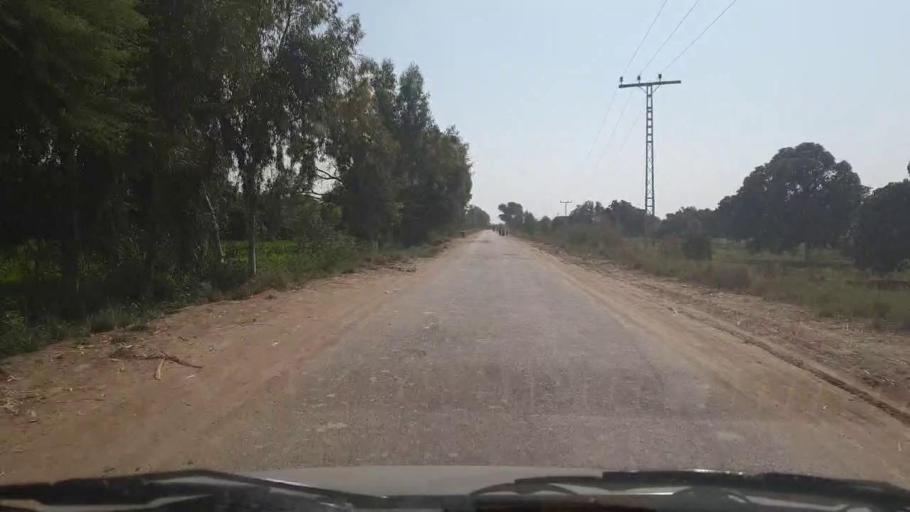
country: PK
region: Sindh
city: Samaro
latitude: 25.2666
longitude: 69.3483
